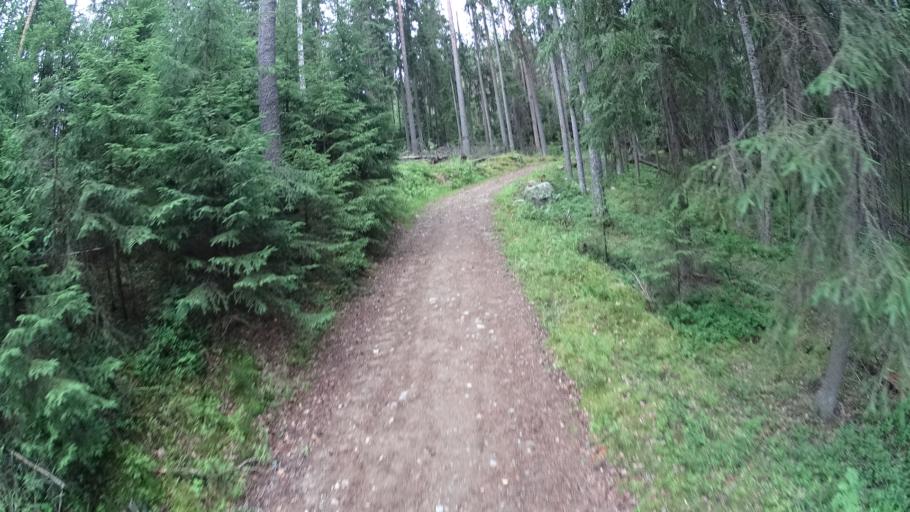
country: FI
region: Southern Savonia
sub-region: Mikkeli
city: Maentyharju
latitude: 61.1765
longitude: 26.8963
